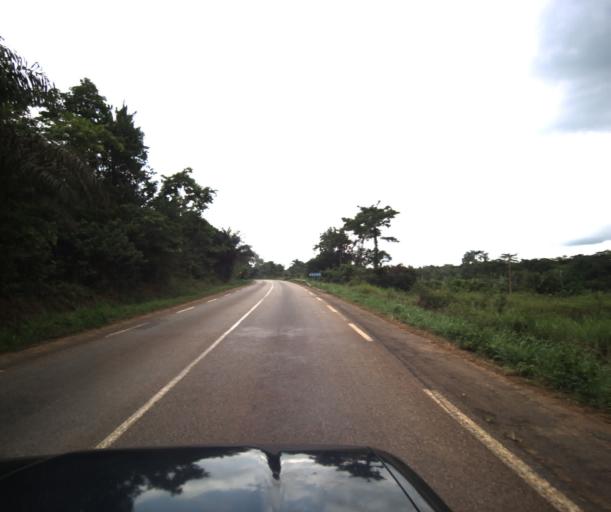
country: CM
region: Centre
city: Eseka
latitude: 3.8717
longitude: 10.6458
